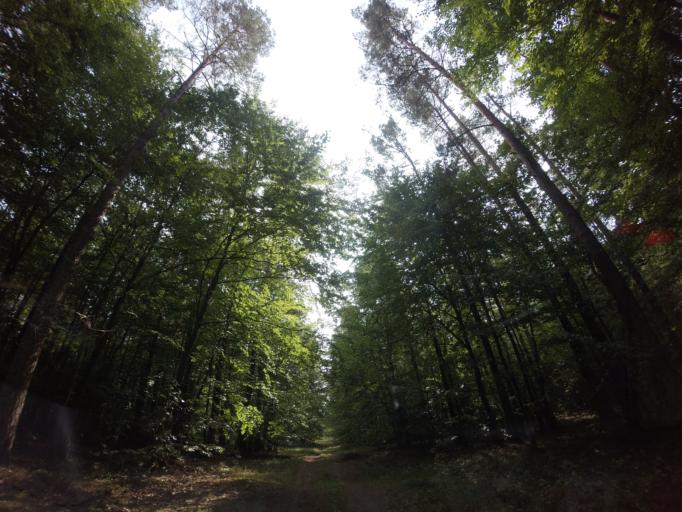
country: PL
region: West Pomeranian Voivodeship
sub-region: Powiat drawski
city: Drawsko Pomorskie
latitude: 53.4599
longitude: 15.7180
